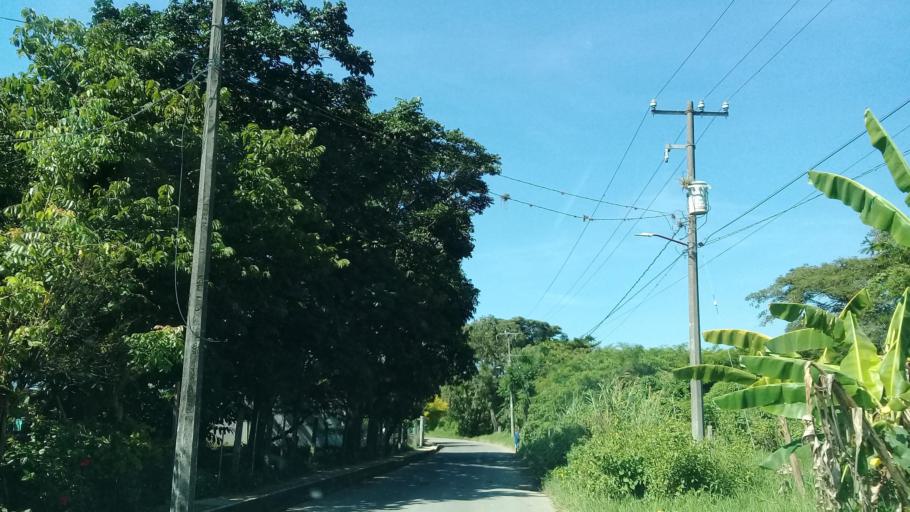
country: MX
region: Veracruz
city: Amatlan de los Reyes
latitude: 18.8542
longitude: -96.9104
